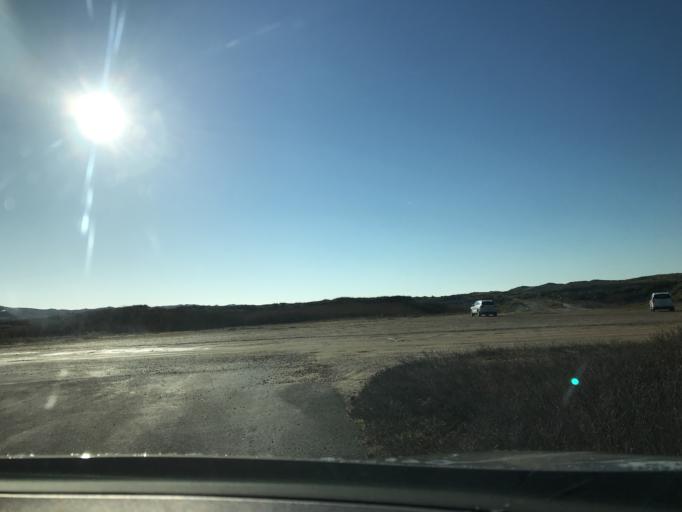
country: DK
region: South Denmark
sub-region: Varde Kommune
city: Oksbol
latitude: 55.7927
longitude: 8.1815
